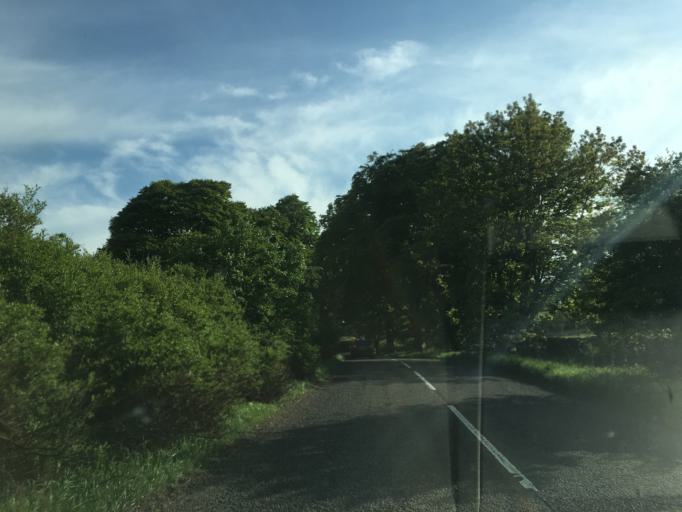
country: GB
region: Scotland
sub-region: The Scottish Borders
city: West Linton
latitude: 55.7091
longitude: -3.3525
